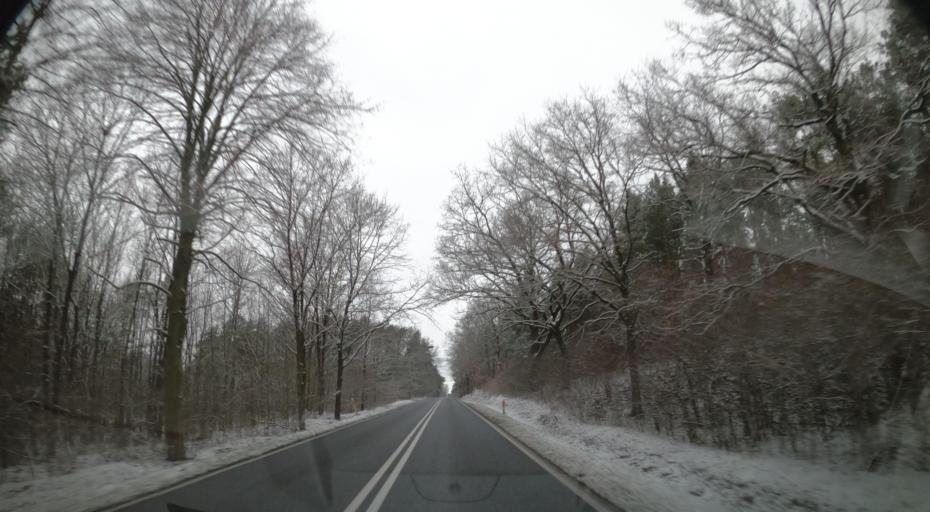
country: PL
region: Masovian Voivodeship
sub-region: Powiat plocki
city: Nowy Duninow
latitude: 52.5844
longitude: 19.5223
